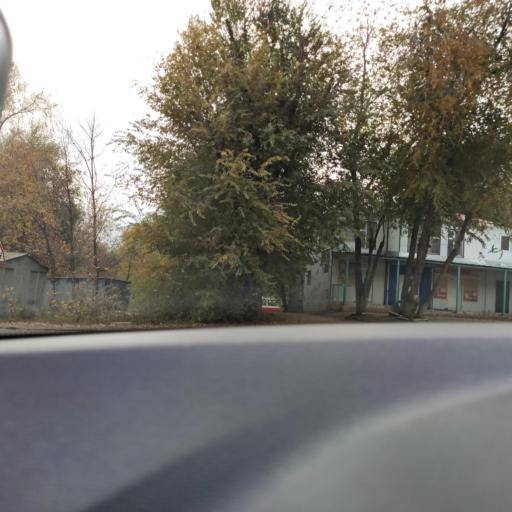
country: RU
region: Samara
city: Samara
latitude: 53.2418
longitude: 50.2564
